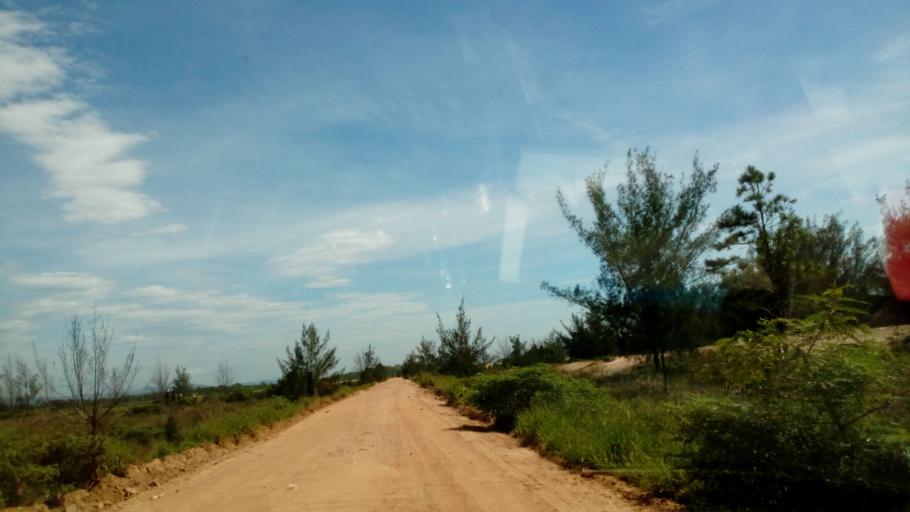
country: BR
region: Santa Catarina
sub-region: Laguna
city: Laguna
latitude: -28.4487
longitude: -48.7638
